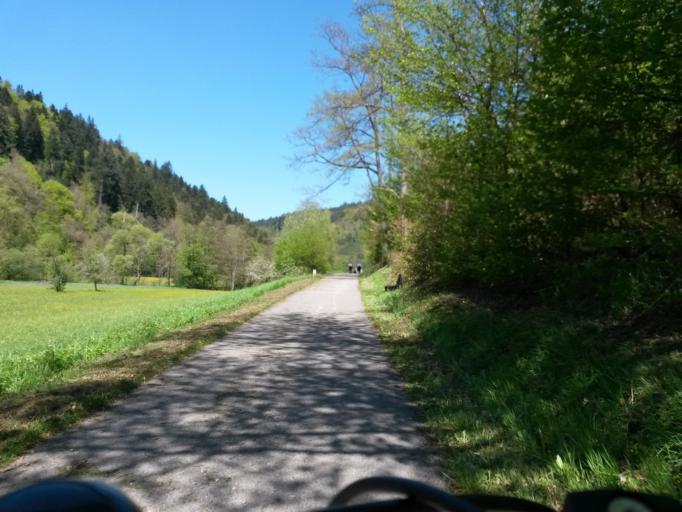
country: DE
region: Baden-Wuerttemberg
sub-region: Karlsruhe Region
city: Unterreichenbach
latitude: 48.8055
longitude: 8.7218
